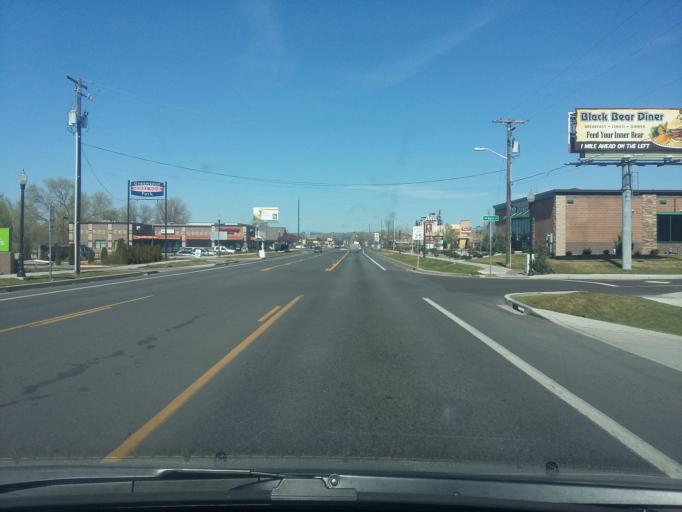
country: US
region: Oregon
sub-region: Jefferson County
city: Madras
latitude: 44.6192
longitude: -121.1329
